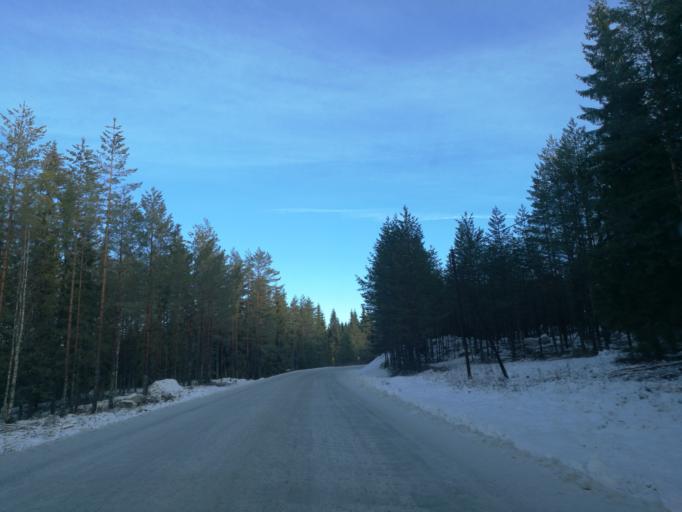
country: NO
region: Hedmark
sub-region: Grue
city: Kirkenaer
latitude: 60.3279
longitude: 12.2843
